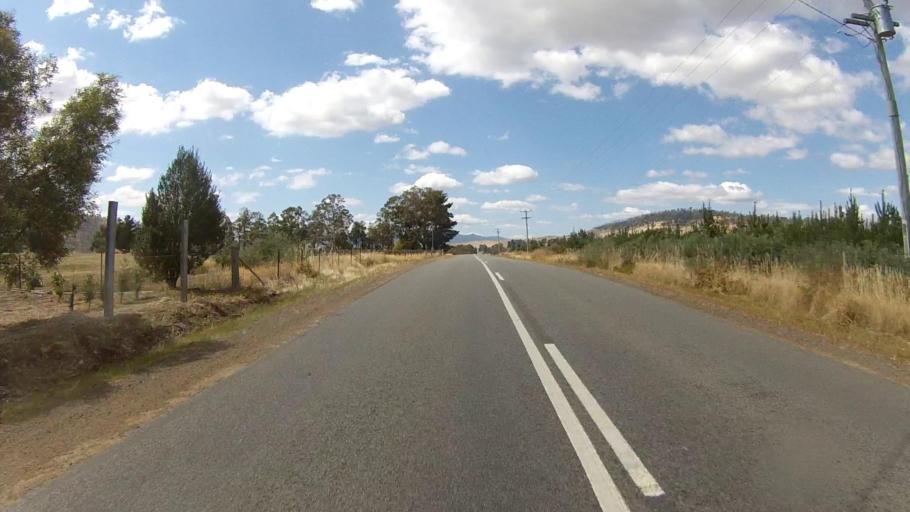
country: AU
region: Tasmania
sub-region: Derwent Valley
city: New Norfolk
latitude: -42.6835
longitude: 146.8228
